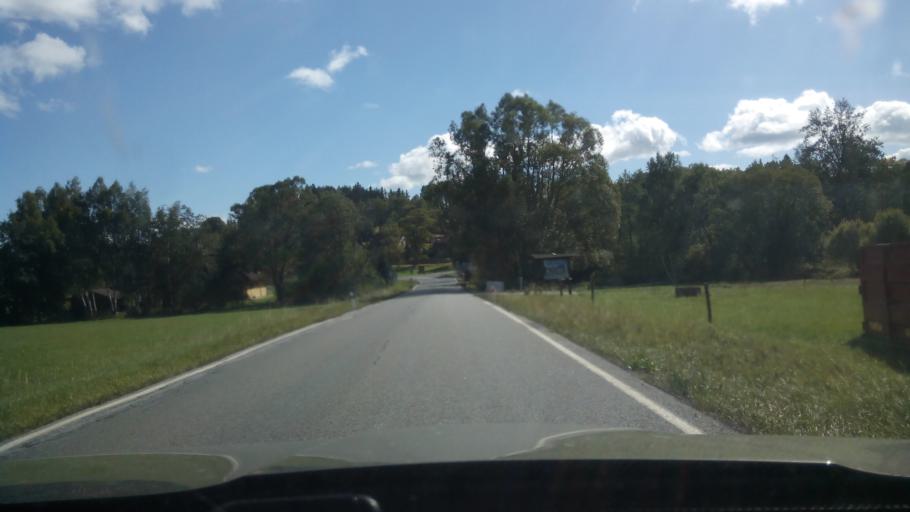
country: CZ
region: Jihocesky
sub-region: Okres Prachatice
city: Stachy
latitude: 49.1034
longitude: 13.6589
